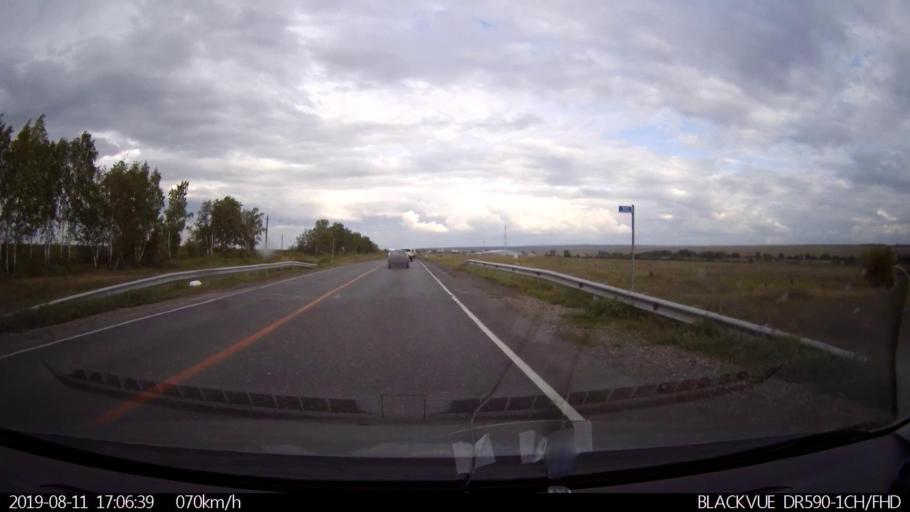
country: RU
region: Ulyanovsk
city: Mayna
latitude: 54.2943
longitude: 47.8100
